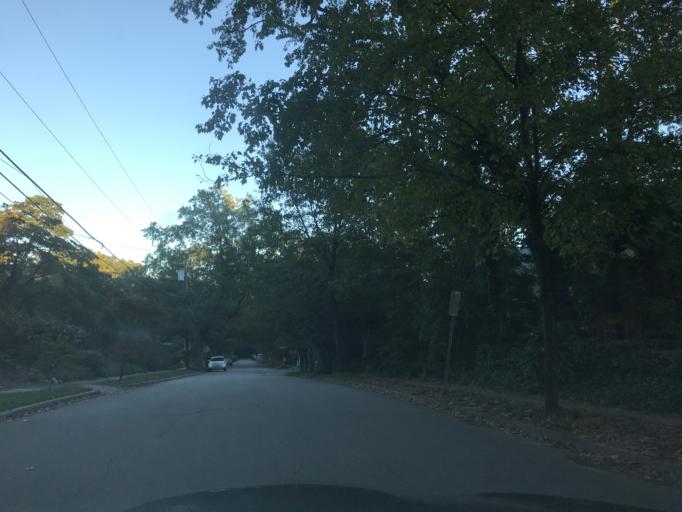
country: US
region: North Carolina
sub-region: Wake County
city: West Raleigh
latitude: 35.7881
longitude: -78.6587
